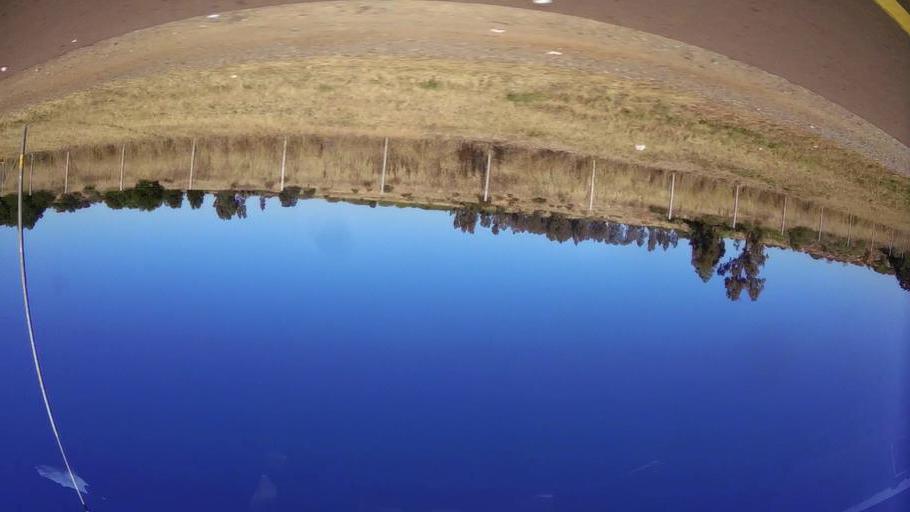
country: ZA
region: Gauteng
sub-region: City of Tshwane Metropolitan Municipality
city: Centurion
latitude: -25.8154
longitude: 28.2344
